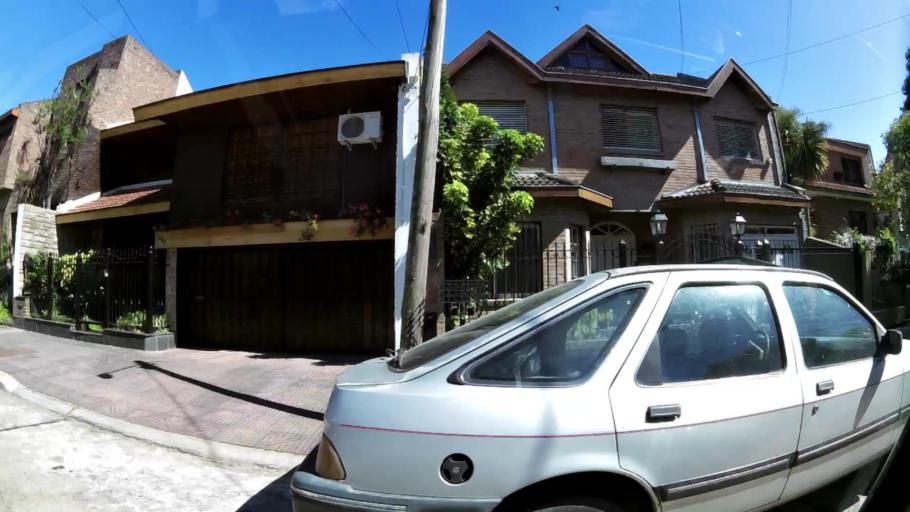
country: AR
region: Buenos Aires
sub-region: Partido de Vicente Lopez
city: Olivos
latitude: -34.5251
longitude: -58.4970
